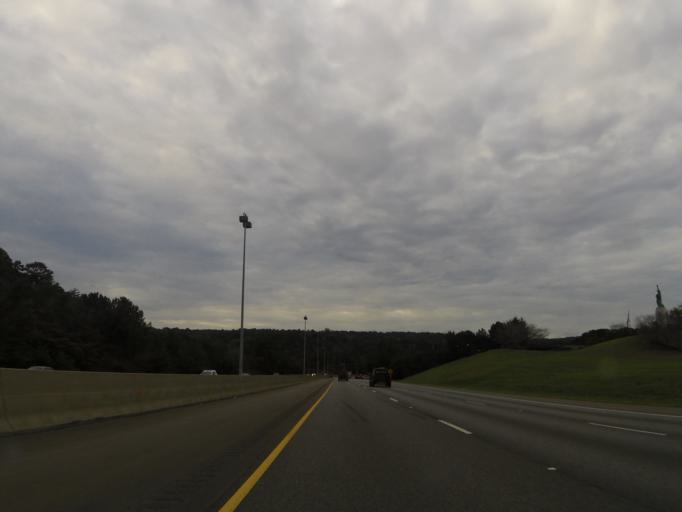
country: US
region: Alabama
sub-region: Jefferson County
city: Cahaba Heights
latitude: 33.4801
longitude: -86.7075
